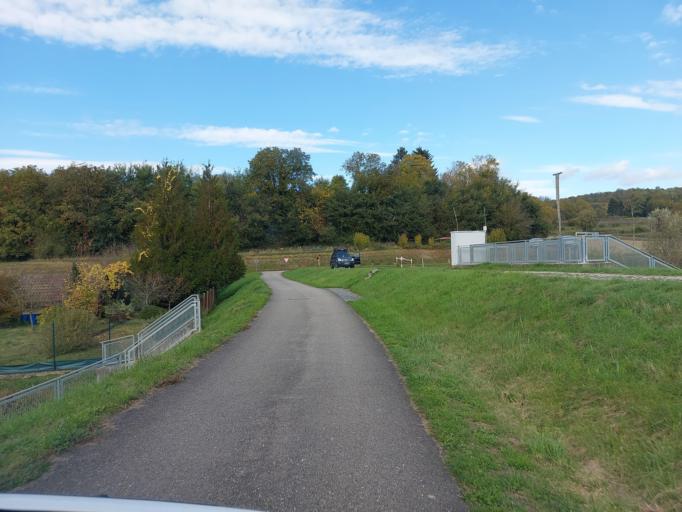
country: DE
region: Baden-Wuerttemberg
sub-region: Freiburg Region
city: Malterdingen
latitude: 48.1659
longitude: 7.7994
